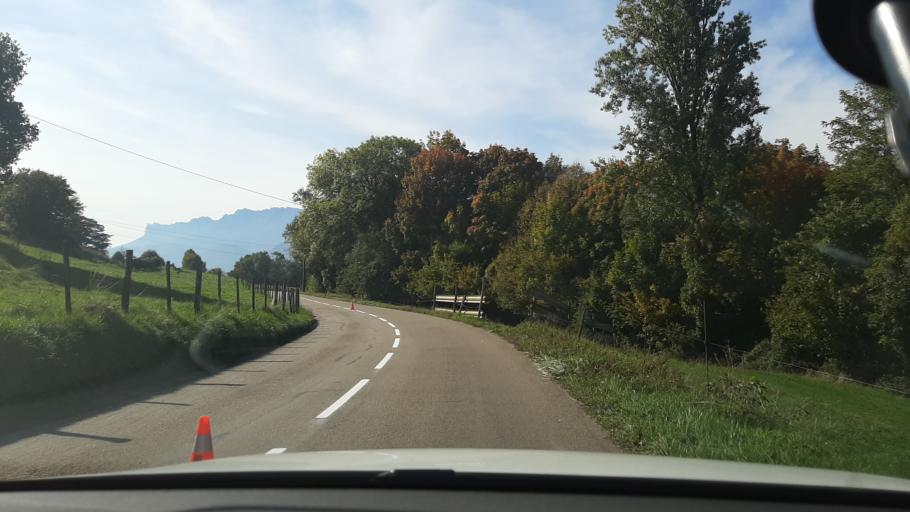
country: FR
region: Rhone-Alpes
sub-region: Departement de l'Isere
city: Pontcharra
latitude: 45.4515
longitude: 6.0588
